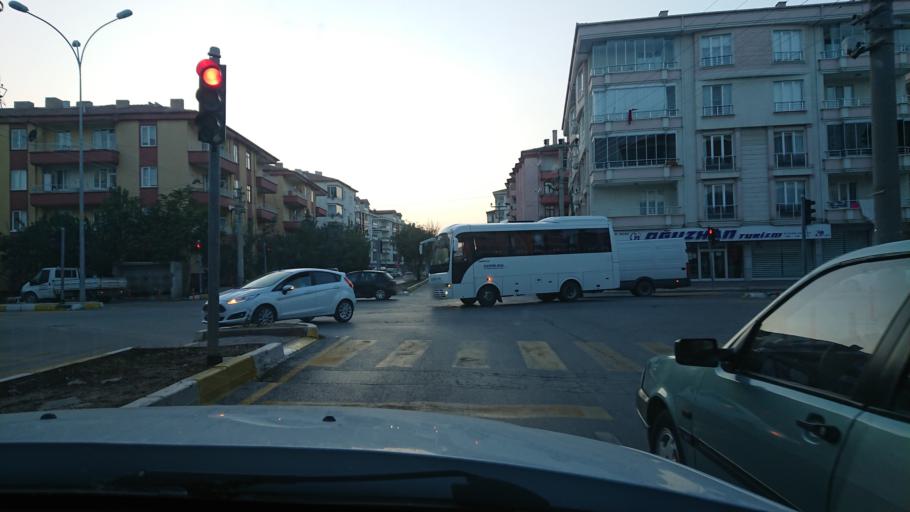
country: TR
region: Aksaray
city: Aksaray
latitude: 38.3607
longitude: 34.0210
